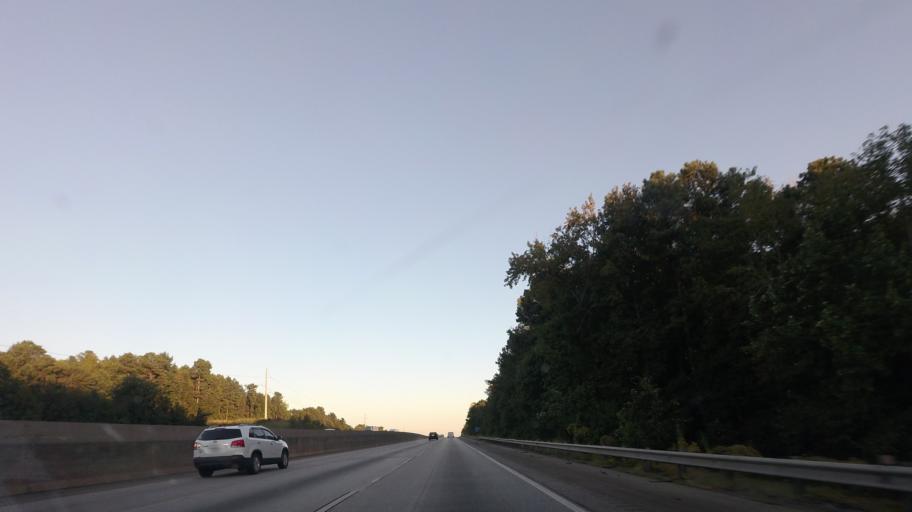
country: US
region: Georgia
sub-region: Monroe County
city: Forsyth
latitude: 33.0045
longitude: -83.8672
